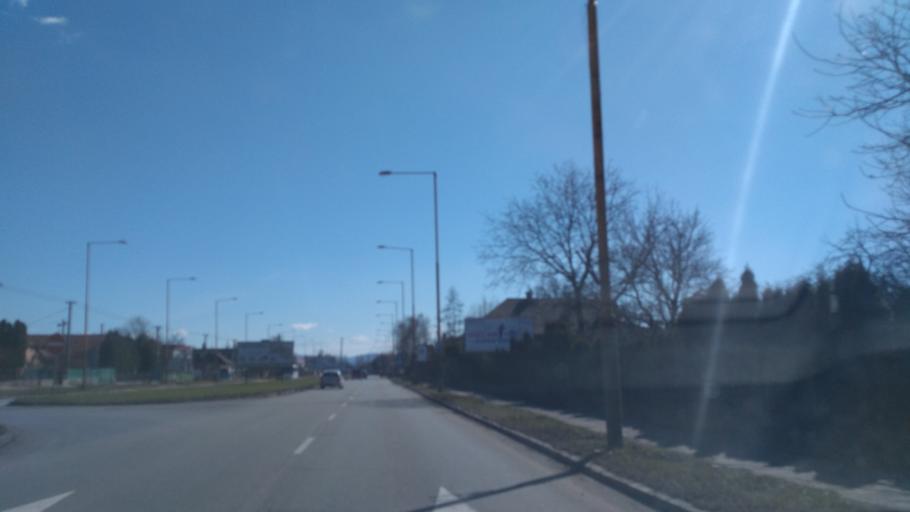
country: SK
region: Kosicky
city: Kosice
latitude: 48.6765
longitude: 21.2693
